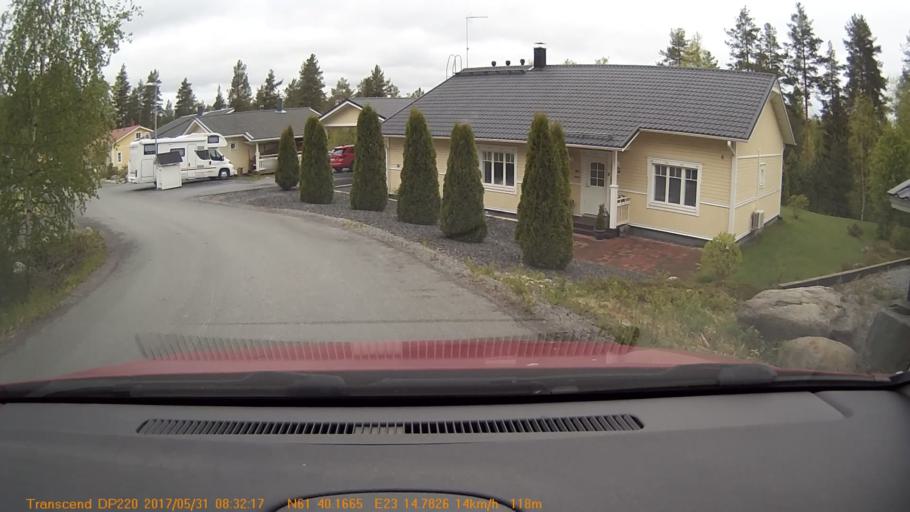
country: FI
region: Pirkanmaa
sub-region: Tampere
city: Viljakkala
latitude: 61.6696
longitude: 23.2463
